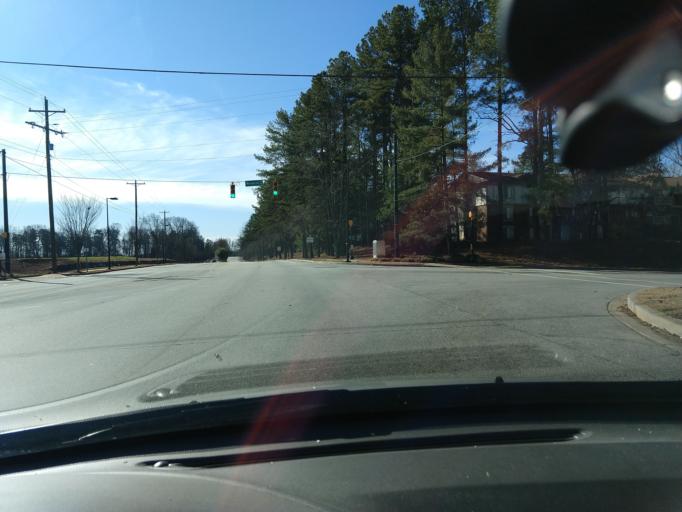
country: US
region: South Carolina
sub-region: Greenville County
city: Mauldin
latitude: 34.7984
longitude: -82.3465
